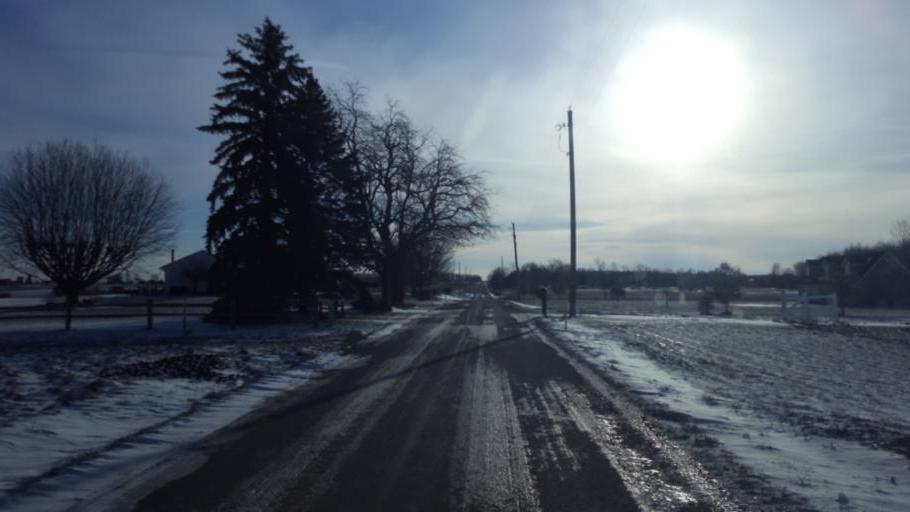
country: US
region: Ohio
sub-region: Morrow County
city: Mount Gilead
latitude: 40.6253
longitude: -82.8329
